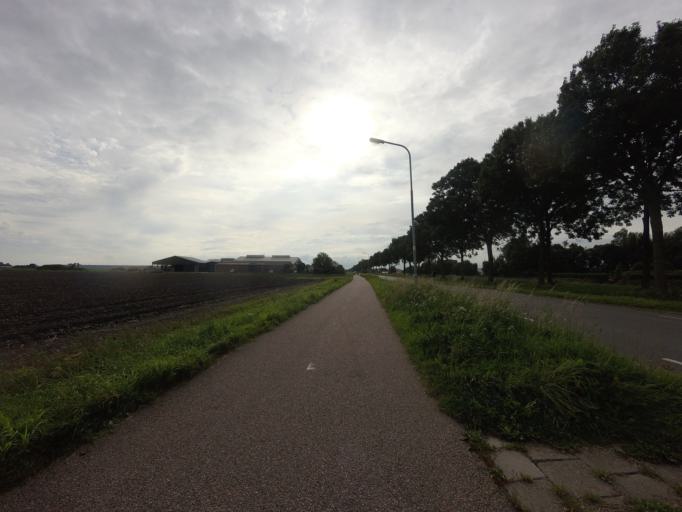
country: NL
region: North Holland
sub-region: Gemeente Medemblik
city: Medemblik
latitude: 52.7193
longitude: 5.1760
